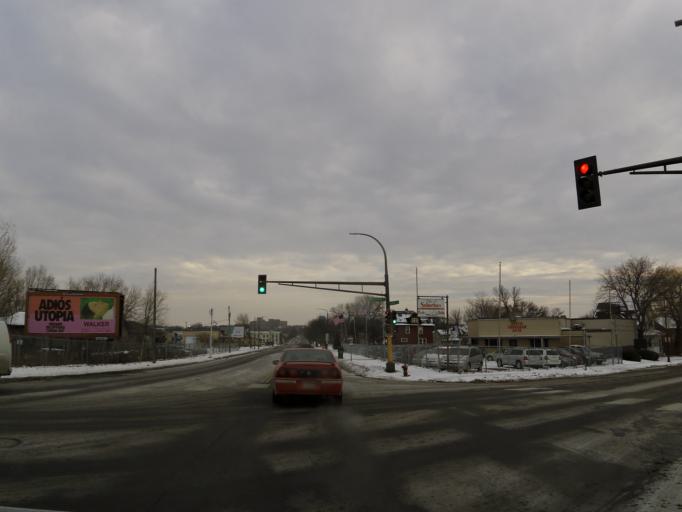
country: US
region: Minnesota
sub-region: Ramsey County
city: Saint Paul
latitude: 44.9646
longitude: -93.1163
